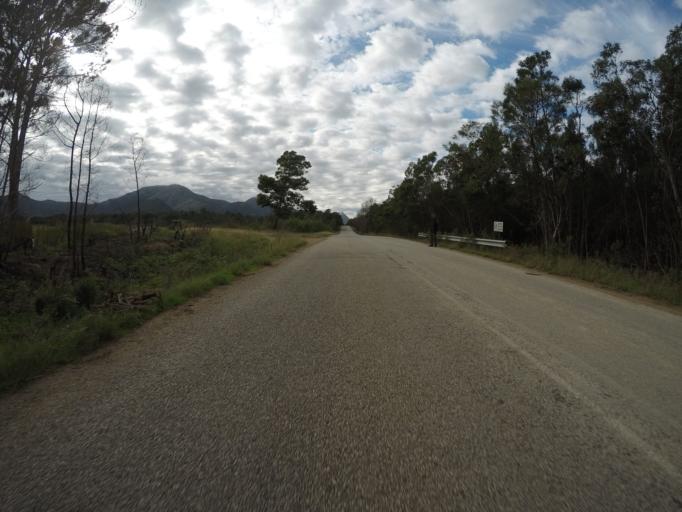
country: ZA
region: Eastern Cape
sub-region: Cacadu District Municipality
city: Kareedouw
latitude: -34.0158
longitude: 24.3301
